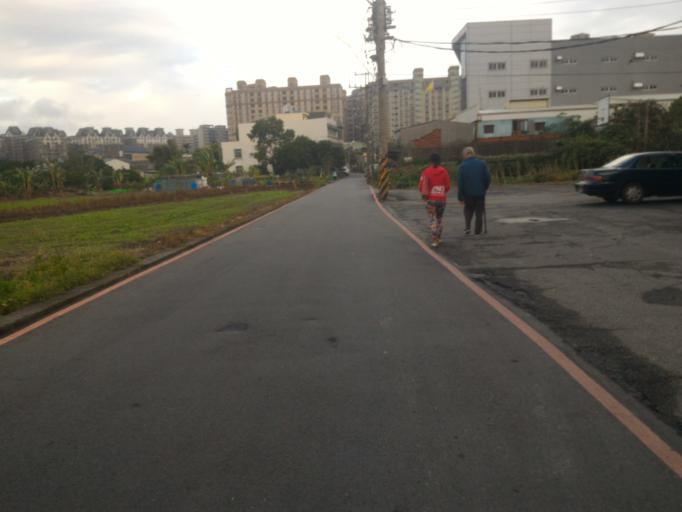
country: TW
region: Taiwan
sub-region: Taoyuan
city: Taoyuan
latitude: 24.9424
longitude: 121.3822
